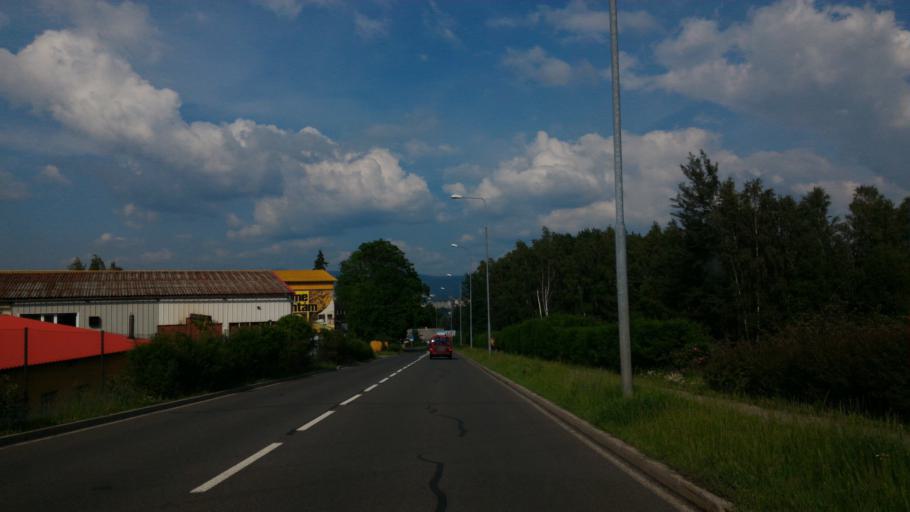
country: CZ
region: Liberecky
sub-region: Okres Liberec
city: Liberec
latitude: 50.7418
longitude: 15.0254
